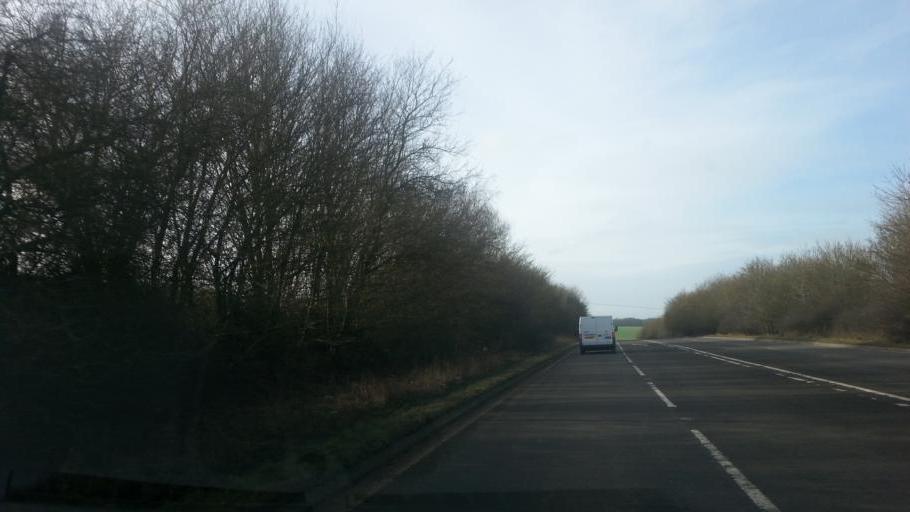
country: GB
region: England
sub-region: District of Rutland
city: Ridlington
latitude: 52.5939
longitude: -0.8378
